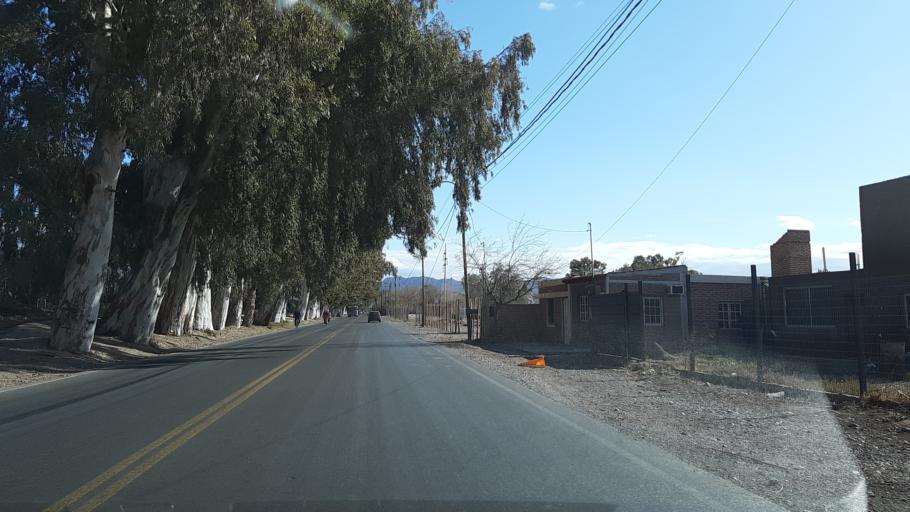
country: AR
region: San Juan
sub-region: Departamento de Rivadavia
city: Rivadavia
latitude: -31.5389
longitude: -68.5987
